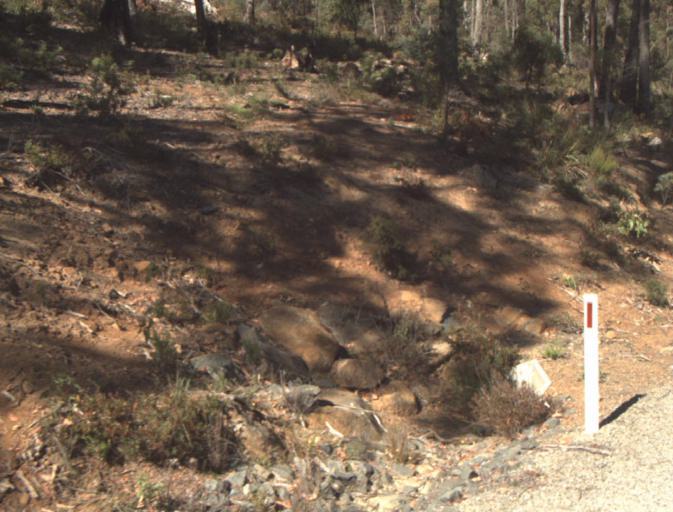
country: AU
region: Tasmania
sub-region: Launceston
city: Mayfield
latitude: -41.3362
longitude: 147.1974
